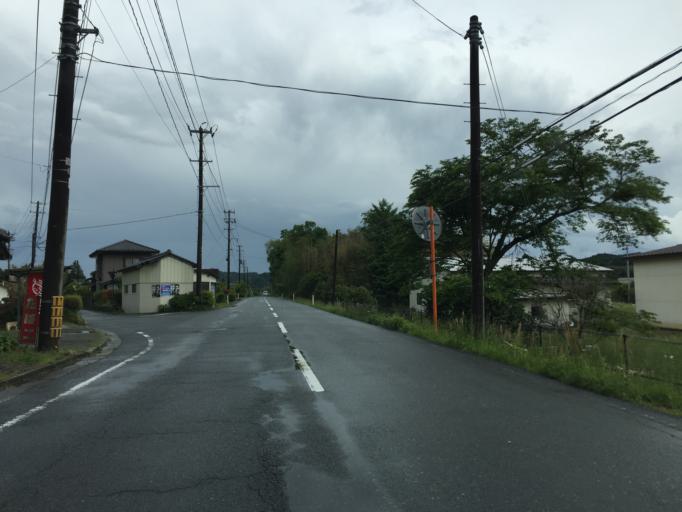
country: JP
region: Ibaraki
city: Kitaibaraki
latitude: 36.9290
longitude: 140.7399
